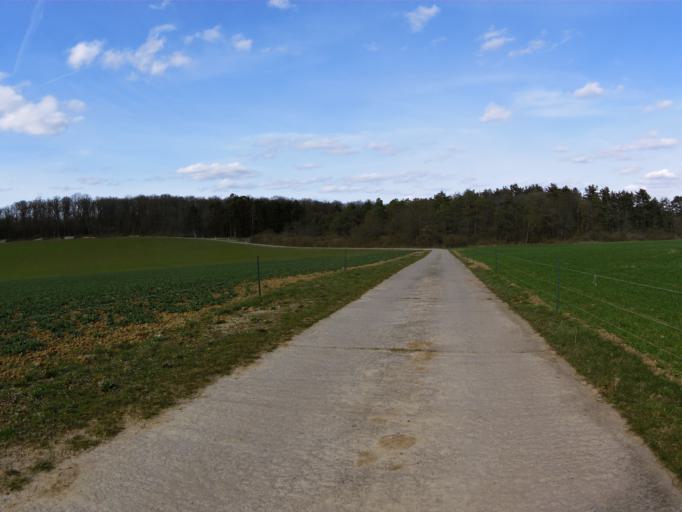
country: DE
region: Bavaria
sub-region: Regierungsbezirk Unterfranken
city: Greussenheim
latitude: 49.8360
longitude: 9.7965
